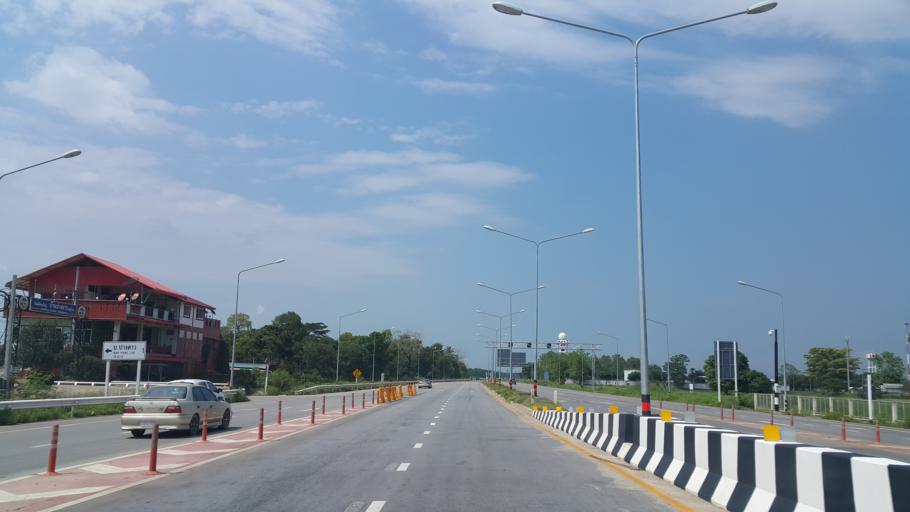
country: TH
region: Chiang Rai
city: Chiang Rai
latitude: 19.9678
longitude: 99.8853
